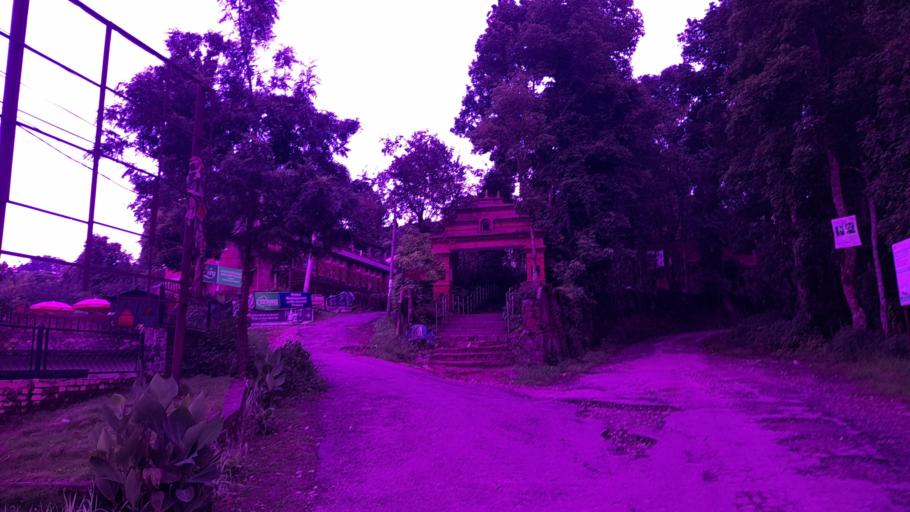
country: NP
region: Central Region
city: Banepa
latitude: 27.6150
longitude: 85.5635
